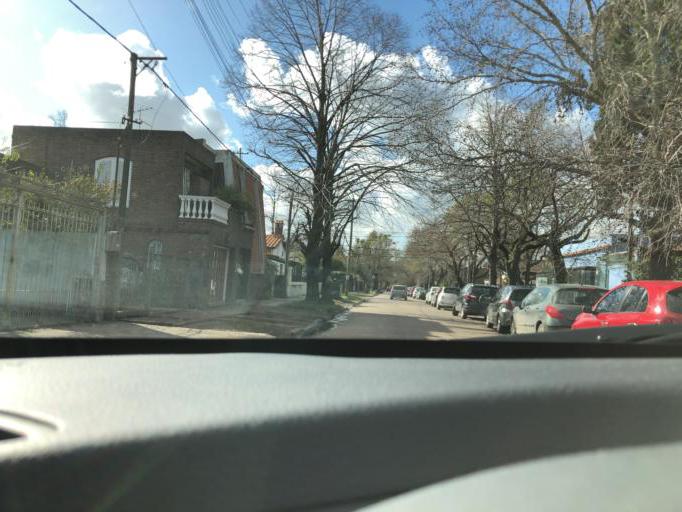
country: AR
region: Buenos Aires
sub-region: Partido de La Plata
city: La Plata
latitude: -34.8700
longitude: -58.0437
